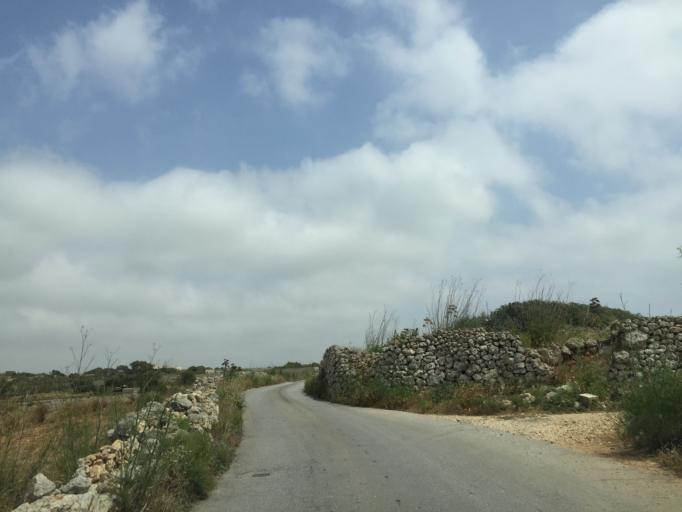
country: MT
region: L-Imgarr
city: Imgarr
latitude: 35.8956
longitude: 14.3580
